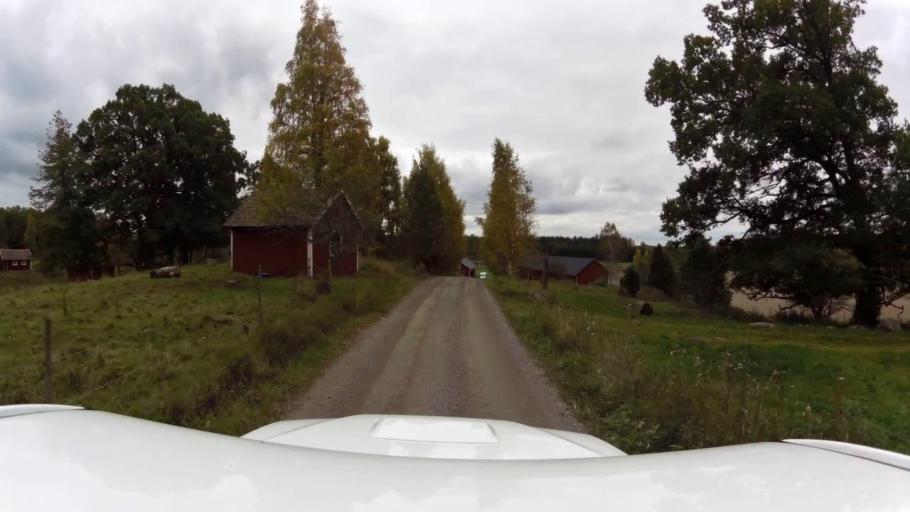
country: SE
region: OEstergoetland
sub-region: Linkopings Kommun
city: Ljungsbro
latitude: 58.5453
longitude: 15.4328
